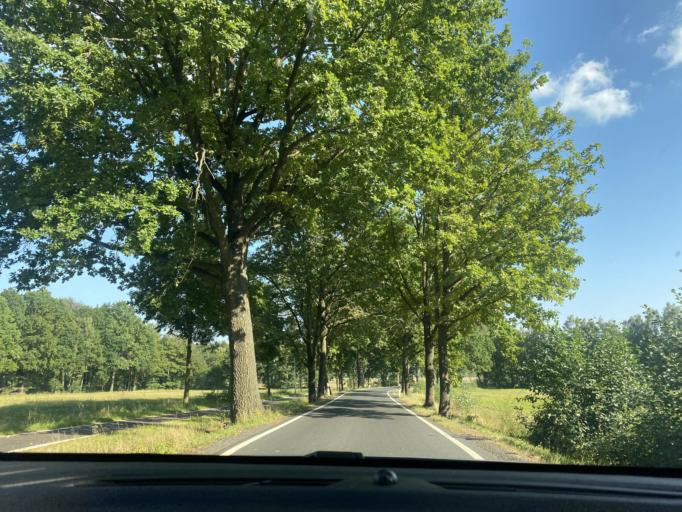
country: DE
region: Saxony
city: Quitzdorf
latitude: 51.2545
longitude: 14.7517
